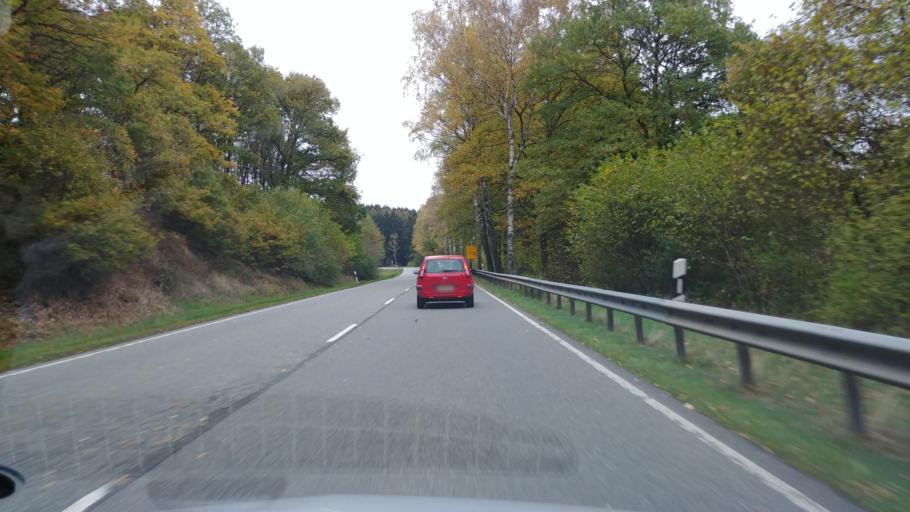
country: DE
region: Rheinland-Pfalz
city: Hilscheid
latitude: 49.7265
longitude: 7.0040
